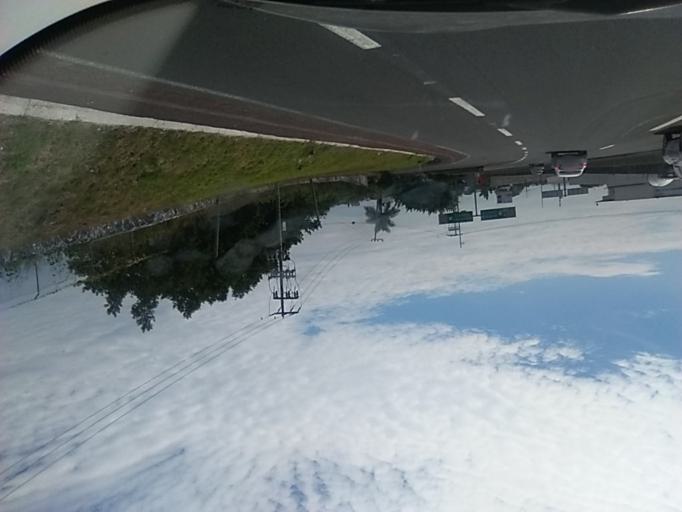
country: MX
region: Morelos
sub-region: Tepoztlan
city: Loma Bonita
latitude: 18.9232
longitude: -99.2026
